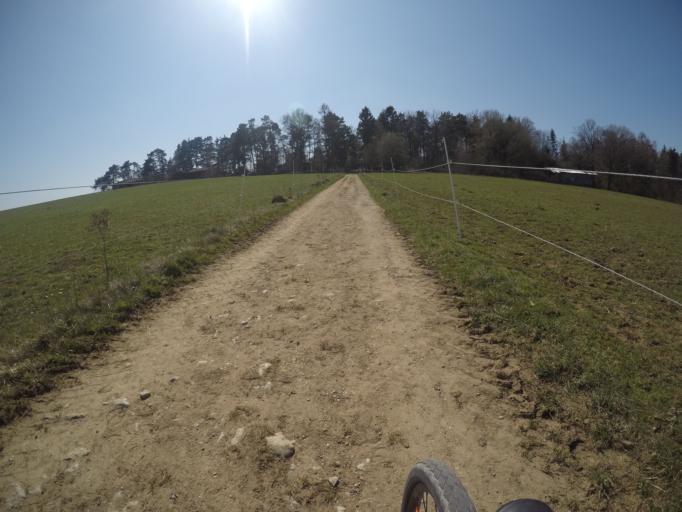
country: DE
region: Baden-Wuerttemberg
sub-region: Karlsruhe Region
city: Ostelsheim
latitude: 48.7062
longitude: 8.8545
